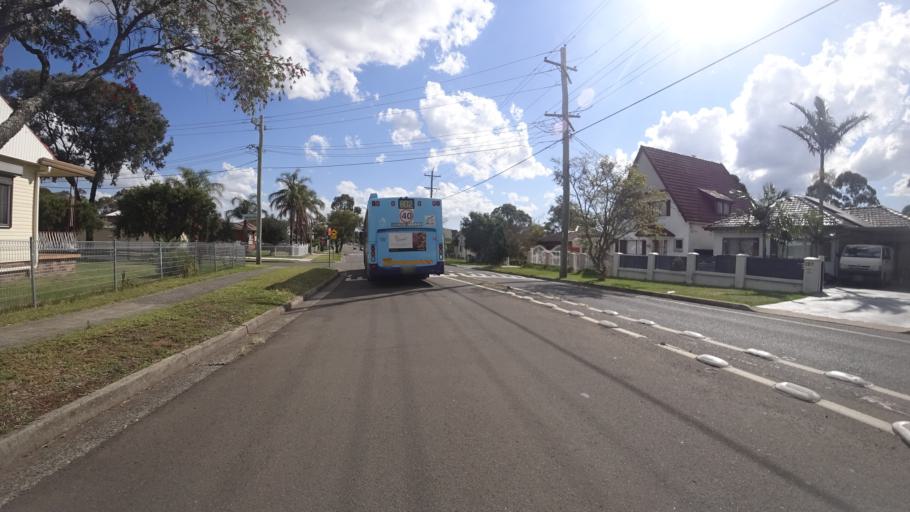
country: AU
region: New South Wales
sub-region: Liverpool
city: Miller
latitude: -33.9226
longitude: 150.9054
